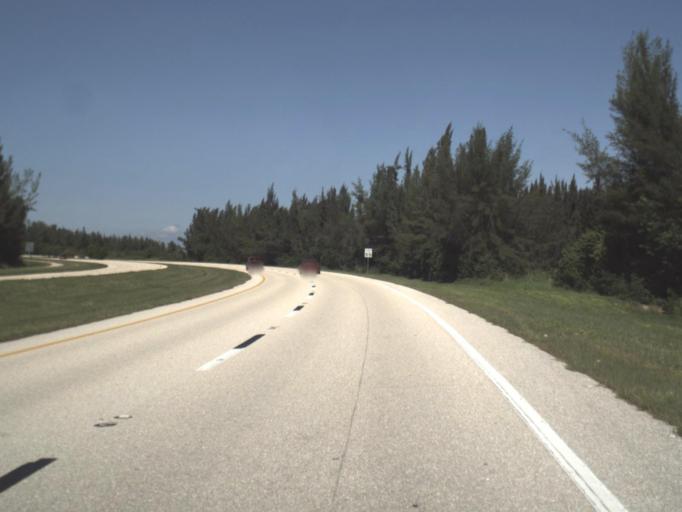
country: US
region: Florida
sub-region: Lee County
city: Pine Island Center
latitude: 26.6118
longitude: -82.0363
